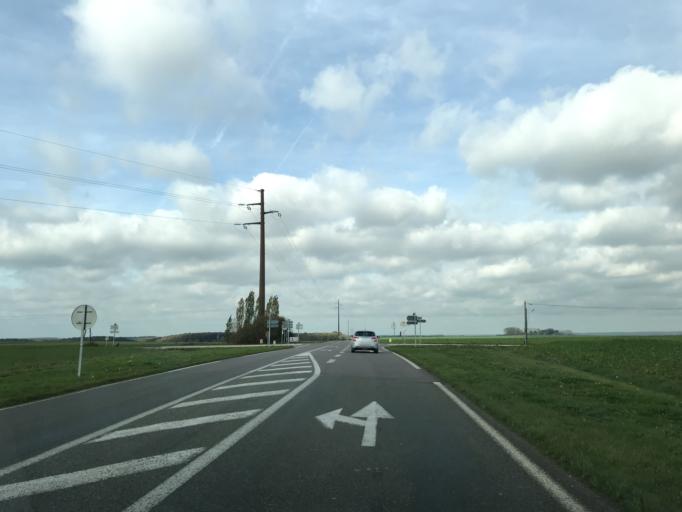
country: FR
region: Haute-Normandie
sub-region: Departement de l'Eure
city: Les Andelys
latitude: 49.3076
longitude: 1.3966
